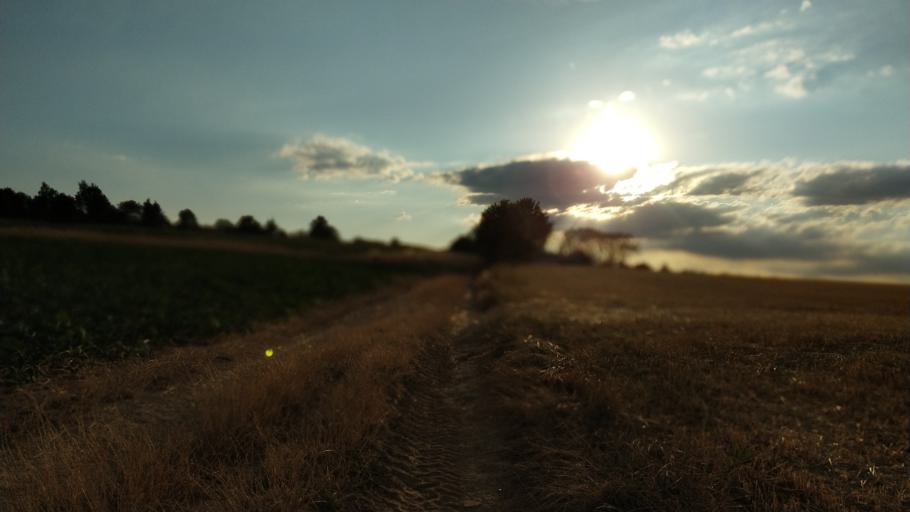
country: BE
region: Flanders
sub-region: Provincie Vlaams-Brabant
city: Bierbeek
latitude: 50.8309
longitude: 4.7392
